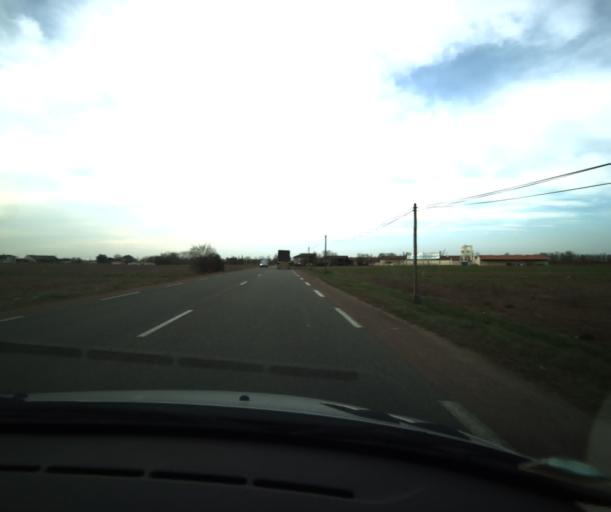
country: FR
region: Midi-Pyrenees
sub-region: Departement du Tarn-et-Garonne
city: Saint-Porquier
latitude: 43.9937
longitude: 1.1893
